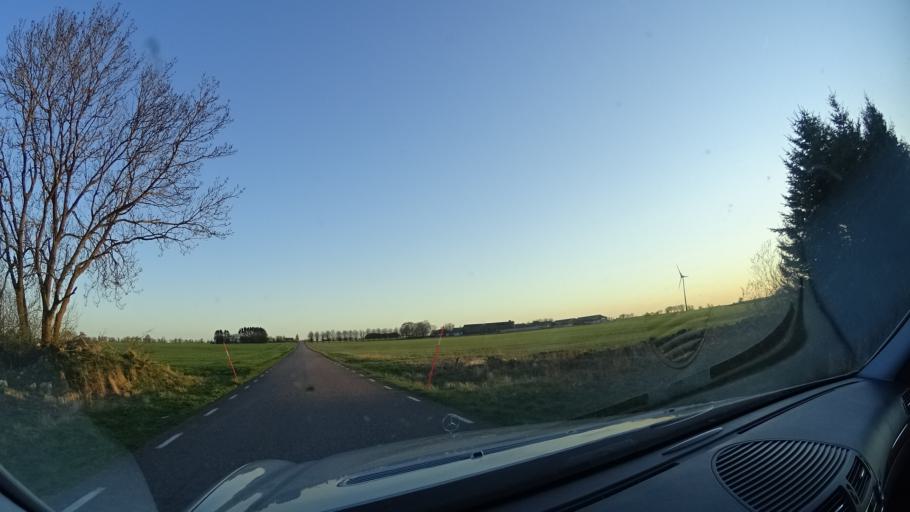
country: SE
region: Skane
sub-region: Hoors Kommun
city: Loberod
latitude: 55.8308
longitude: 13.4538
